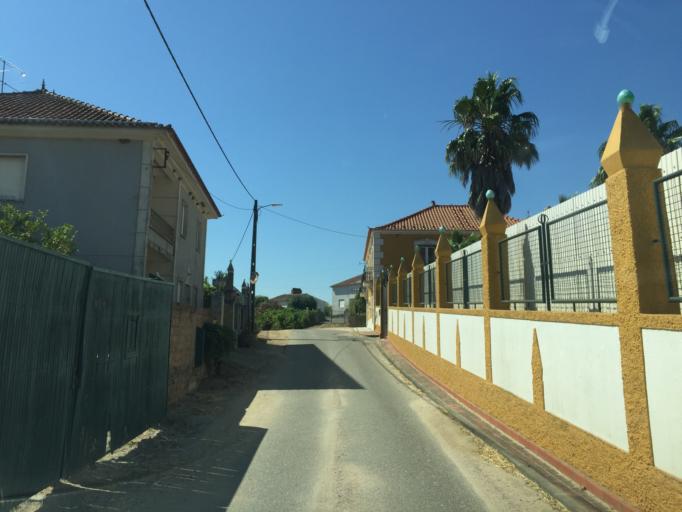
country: PT
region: Santarem
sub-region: Ferreira do Zezere
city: Ferreira do Zezere
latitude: 39.5882
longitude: -8.2790
